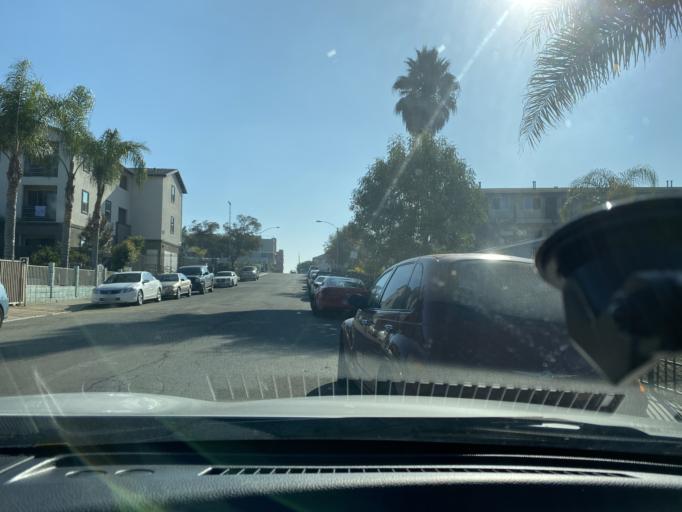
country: US
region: California
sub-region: San Diego County
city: National City
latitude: 32.7053
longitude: -117.0868
